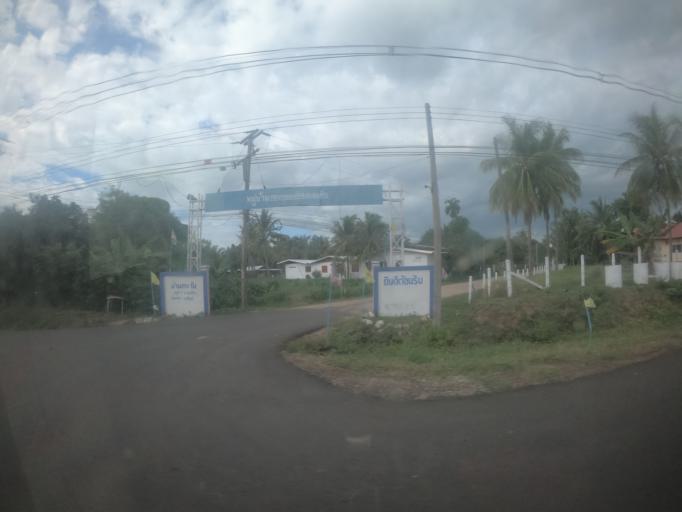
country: TH
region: Surin
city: Prasat
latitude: 14.5646
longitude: 103.4945
